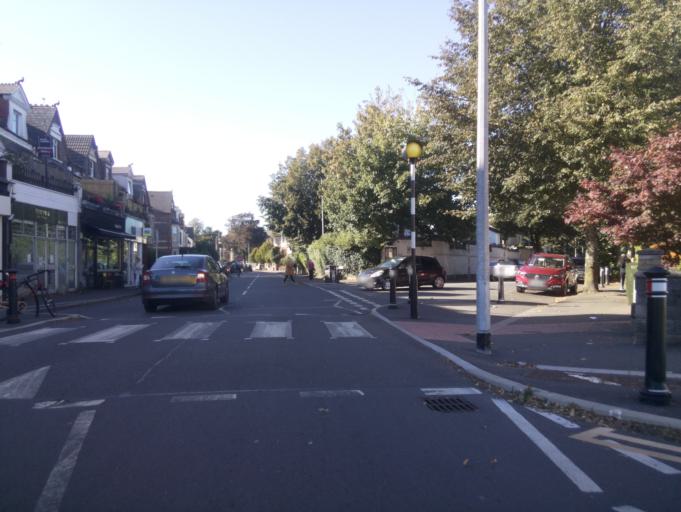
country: GB
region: Wales
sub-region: Cardiff
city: Cardiff
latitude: 51.4846
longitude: -3.2002
